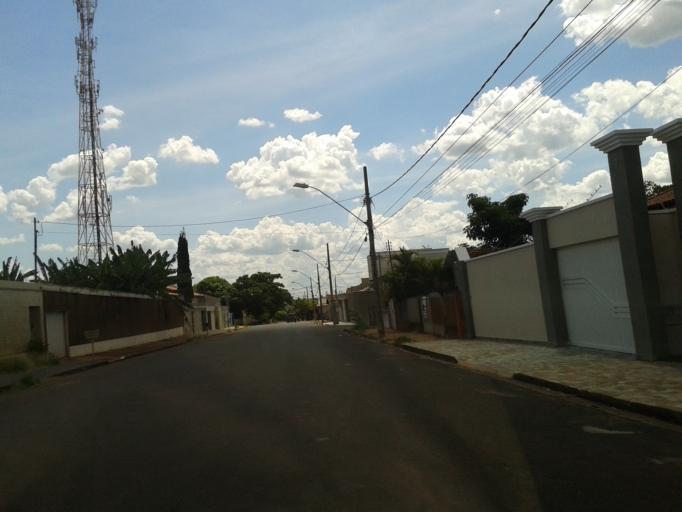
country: BR
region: Minas Gerais
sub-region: Ituiutaba
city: Ituiutaba
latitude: -18.9855
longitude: -49.4651
